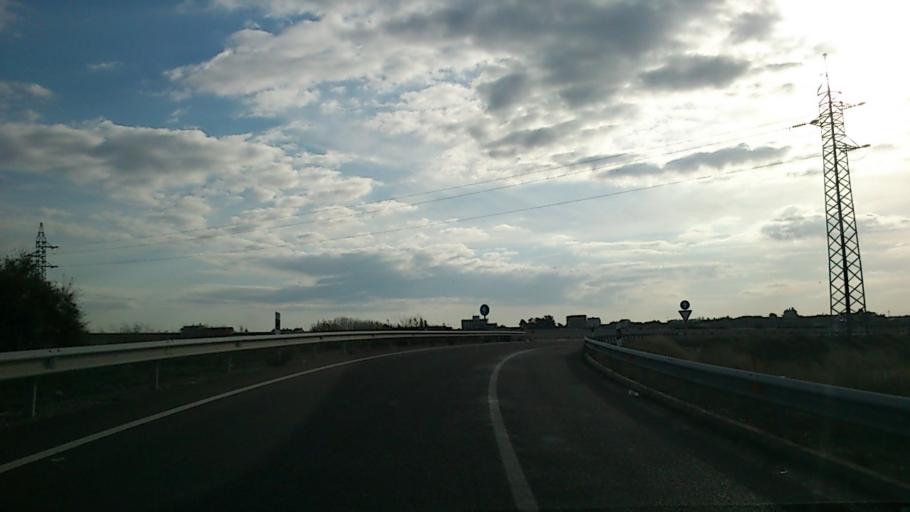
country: ES
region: Aragon
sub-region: Provincia de Zaragoza
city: Zaragoza
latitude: 41.6922
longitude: -0.8359
